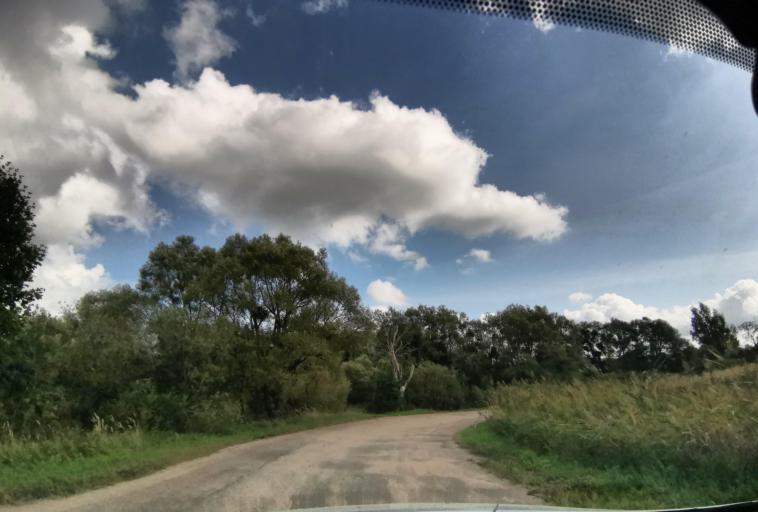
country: PL
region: Warmian-Masurian Voivodeship
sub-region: Powiat goldapski
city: Goldap
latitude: 54.4209
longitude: 22.3981
